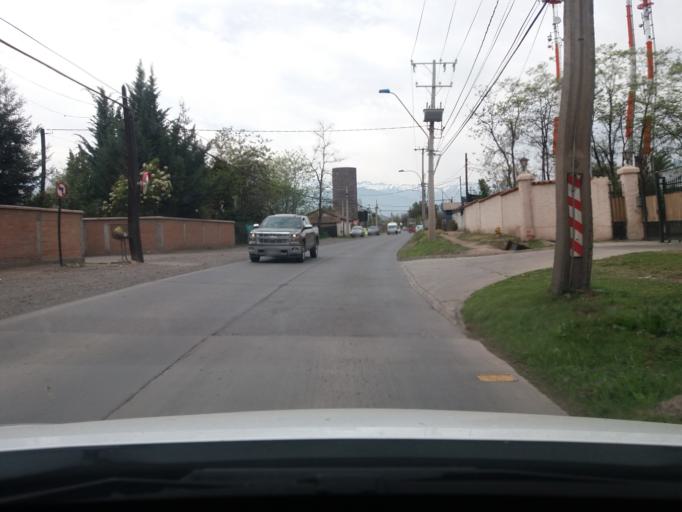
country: CL
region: Valparaiso
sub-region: Provincia de Los Andes
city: Los Andes
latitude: -32.8313
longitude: -70.6169
